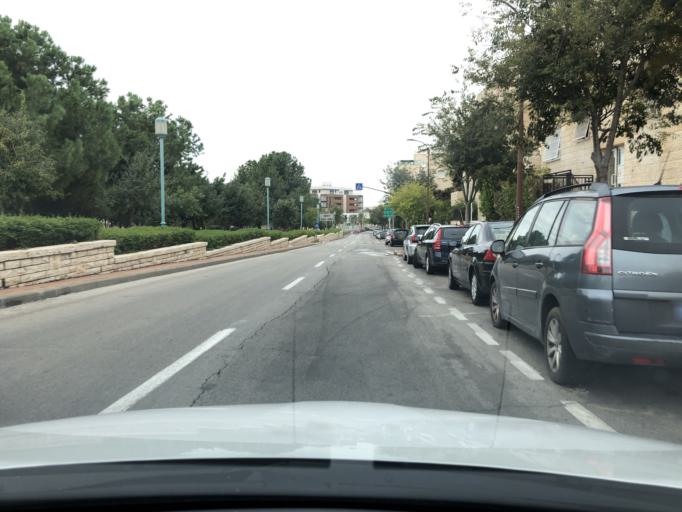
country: IL
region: Central District
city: Modiin
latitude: 31.9029
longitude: 35.0122
